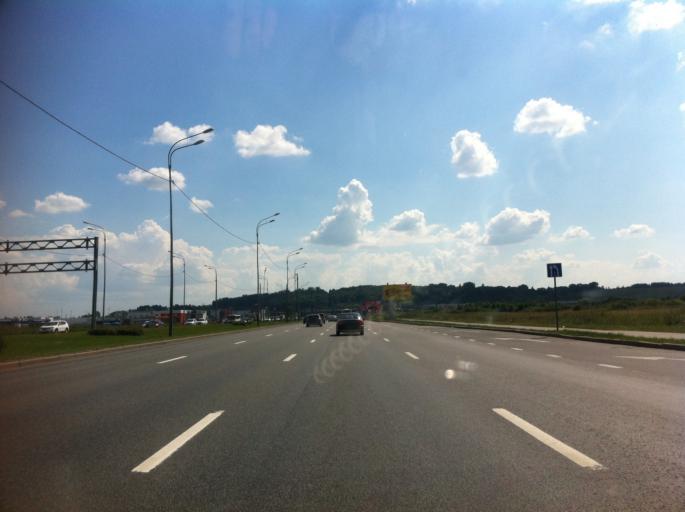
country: RU
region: St.-Petersburg
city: Aleksandrovskaya
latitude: 59.7873
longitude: 30.3247
